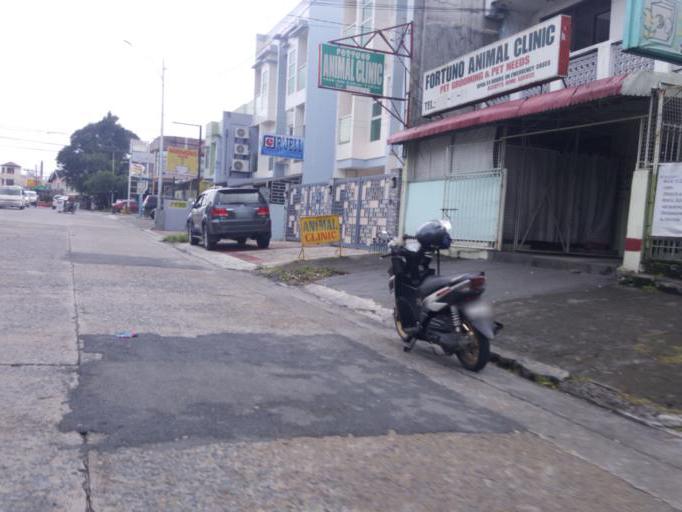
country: PH
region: Calabarzon
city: Bagong Pagasa
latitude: 14.7012
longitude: 121.0227
